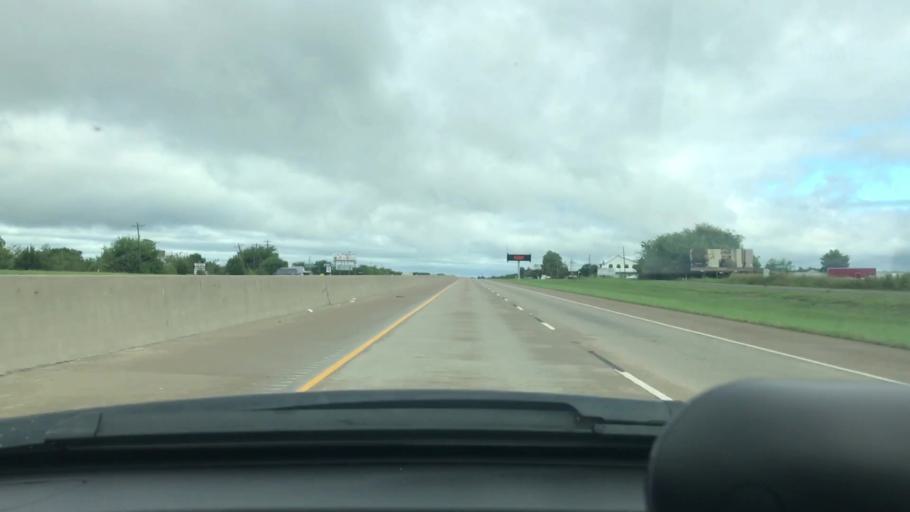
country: US
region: Texas
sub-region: Grayson County
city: Van Alstyne
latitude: 33.4491
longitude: -96.6037
